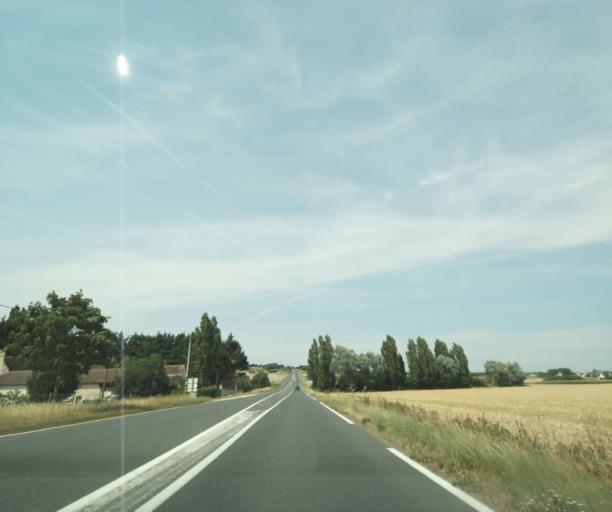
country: FR
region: Centre
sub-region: Departement d'Indre-et-Loire
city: La Celle-Saint-Avant
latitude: 47.0484
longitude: 0.6130
